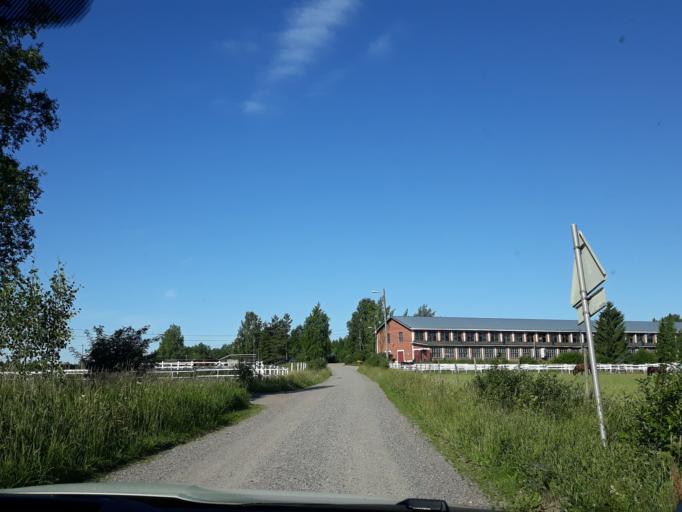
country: FI
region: Uusimaa
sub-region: Helsinki
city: Jaervenpaeae
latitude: 60.5395
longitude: 24.9952
